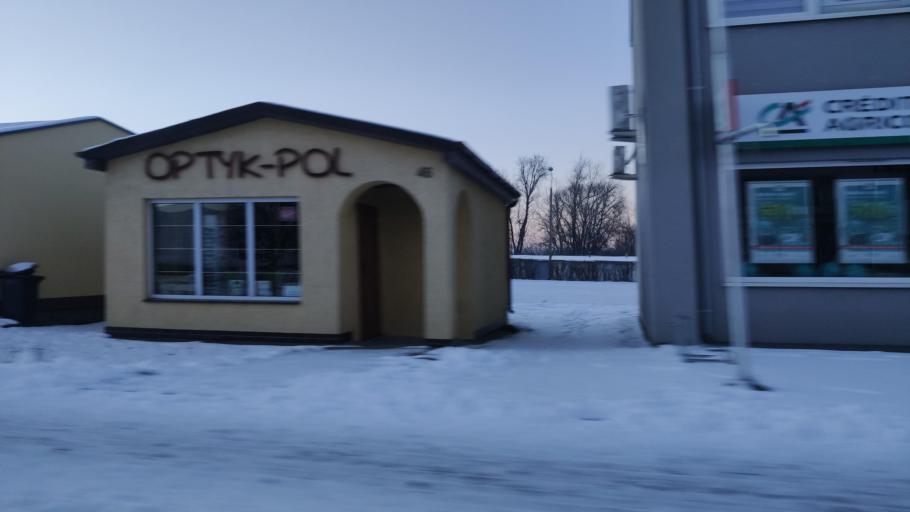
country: PL
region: Kujawsko-Pomorskie
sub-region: Powiat zninski
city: Barcin
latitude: 52.8587
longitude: 17.9429
